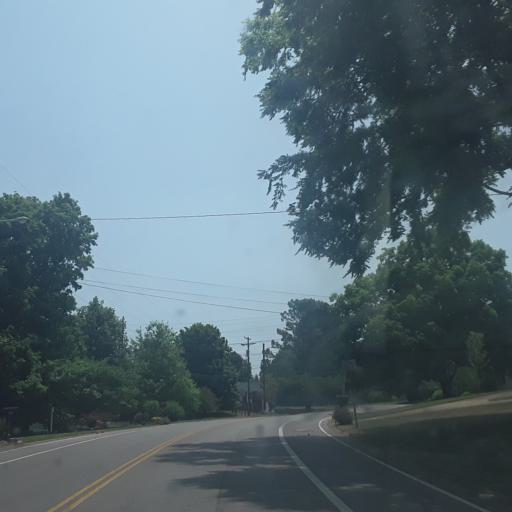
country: US
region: Tennessee
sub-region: Williamson County
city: Brentwood
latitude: 36.0560
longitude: -86.7597
